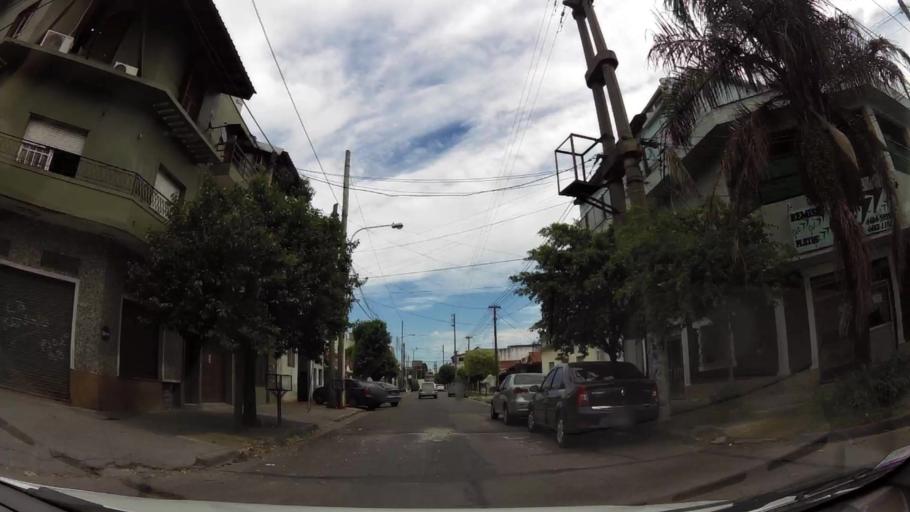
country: AR
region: Buenos Aires
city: San Justo
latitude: -34.6732
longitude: -58.5465
